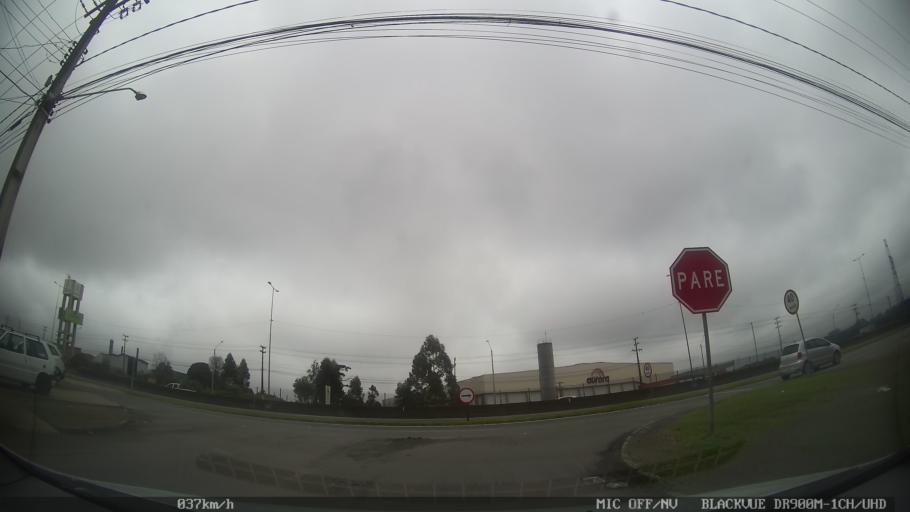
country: BR
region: Parana
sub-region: Sao Jose Dos Pinhais
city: Sao Jose dos Pinhais
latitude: -25.6024
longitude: -49.1725
